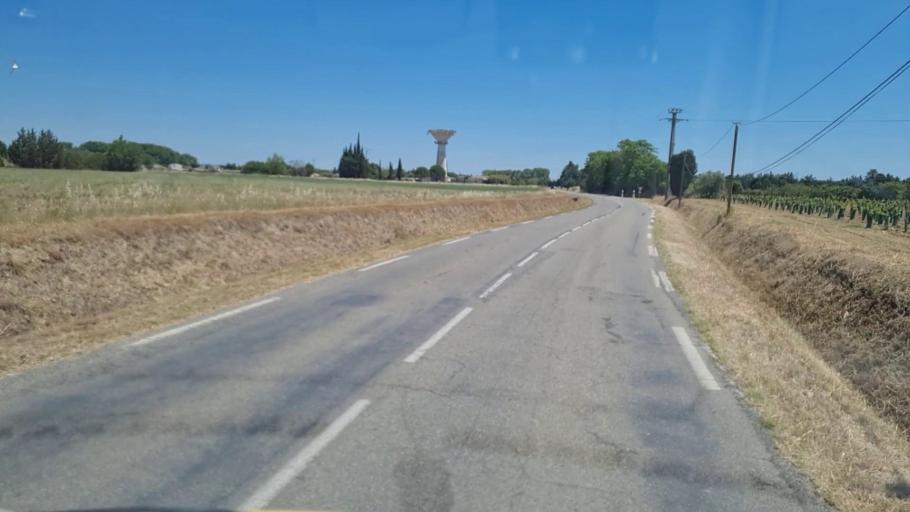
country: FR
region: Languedoc-Roussillon
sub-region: Departement du Gard
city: Aimargues
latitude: 43.6890
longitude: 4.1946
